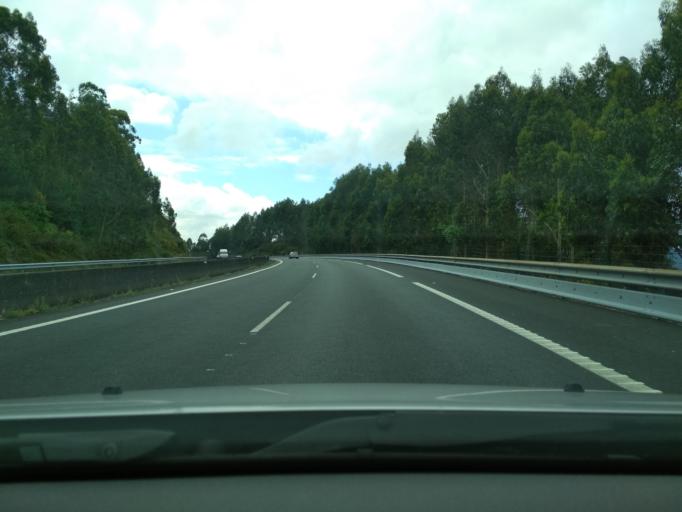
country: ES
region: Galicia
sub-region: Provincia da Coruna
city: Padron
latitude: 42.7849
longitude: -8.6441
